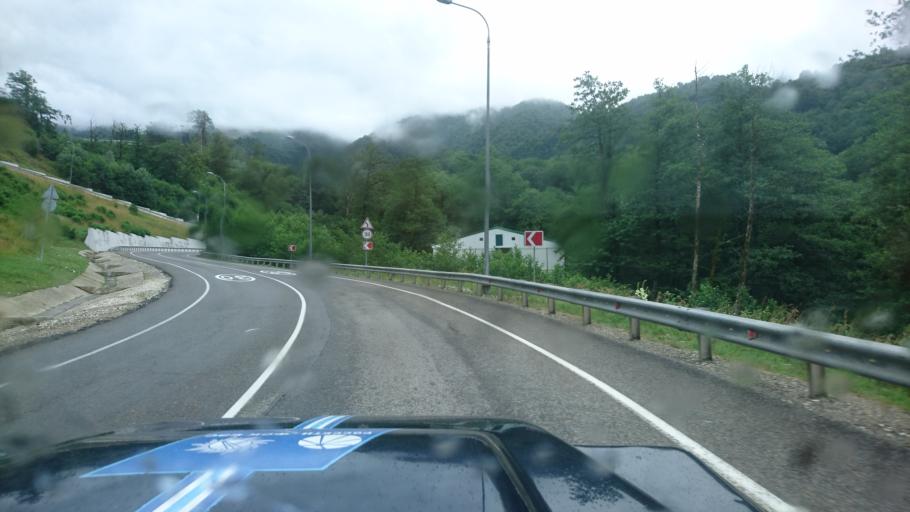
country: RU
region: Krasnodarskiy
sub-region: Sochi City
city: Krasnaya Polyana
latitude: 43.6734
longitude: 40.2857
